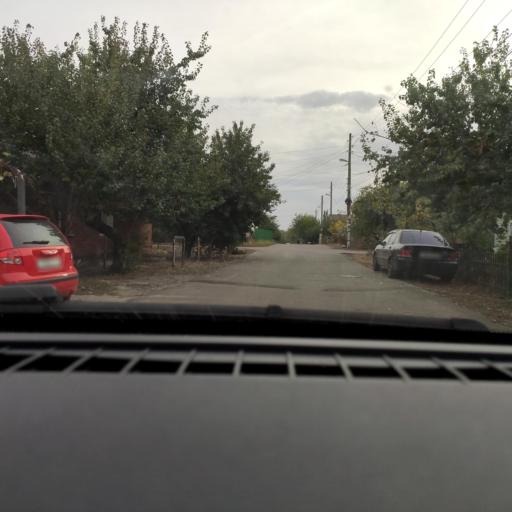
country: RU
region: Voronezj
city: Voronezh
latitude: 51.6700
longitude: 39.2659
